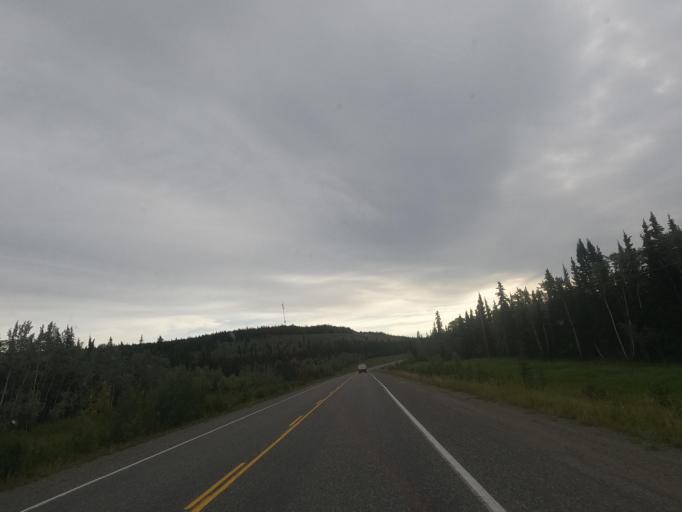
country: CA
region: Yukon
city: Whitehorse
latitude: 60.7618
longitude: -136.1065
